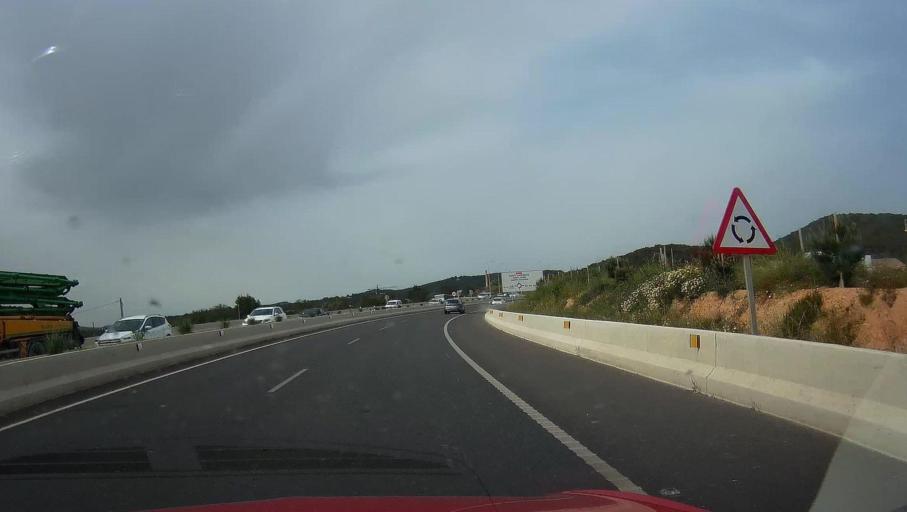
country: ES
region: Balearic Islands
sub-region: Illes Balears
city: Ibiza
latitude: 38.9499
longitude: 1.4436
